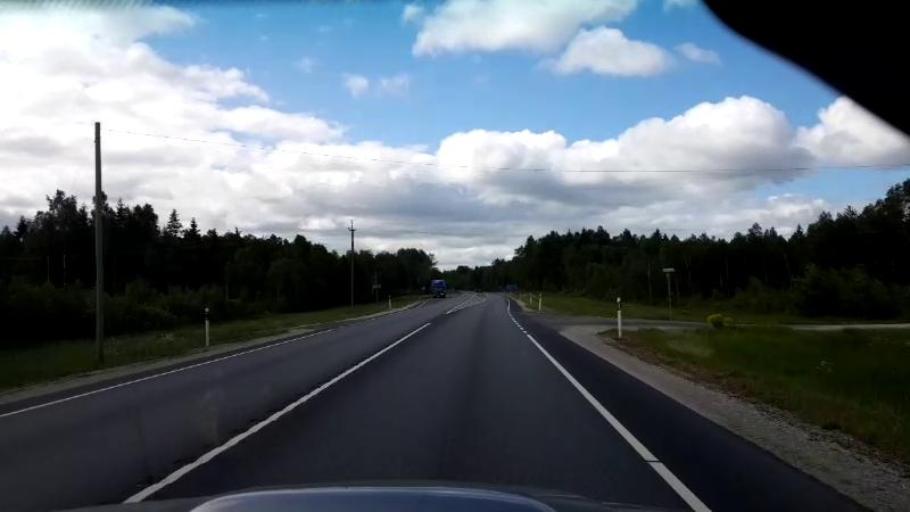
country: EE
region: Raplamaa
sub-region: Maerjamaa vald
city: Marjamaa
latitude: 59.0472
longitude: 24.4437
